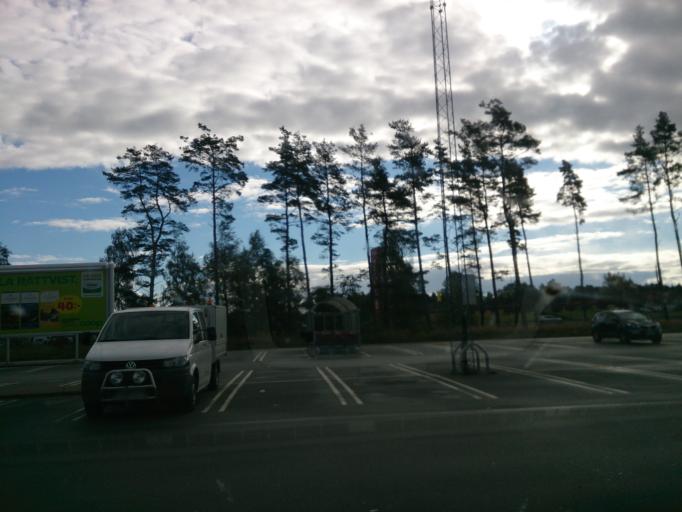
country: SE
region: Skane
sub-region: Sjobo Kommun
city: Sjoebo
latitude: 55.6362
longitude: 13.6807
